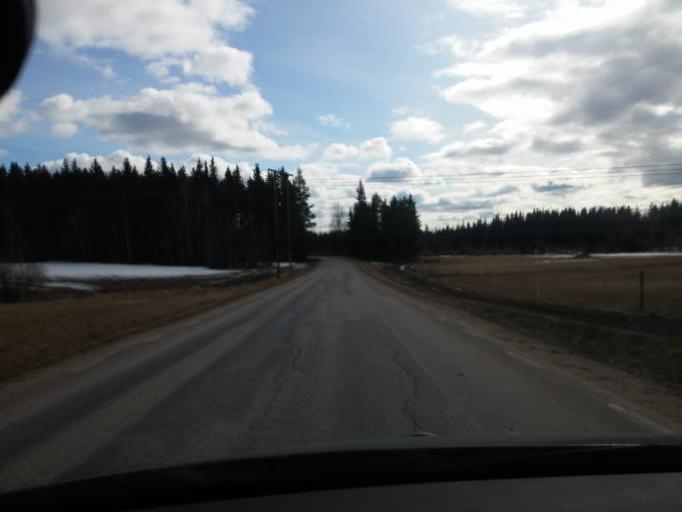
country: SE
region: Gaevleborg
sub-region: Ljusdals Kommun
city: Ljusdal
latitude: 61.8139
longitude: 16.1500
